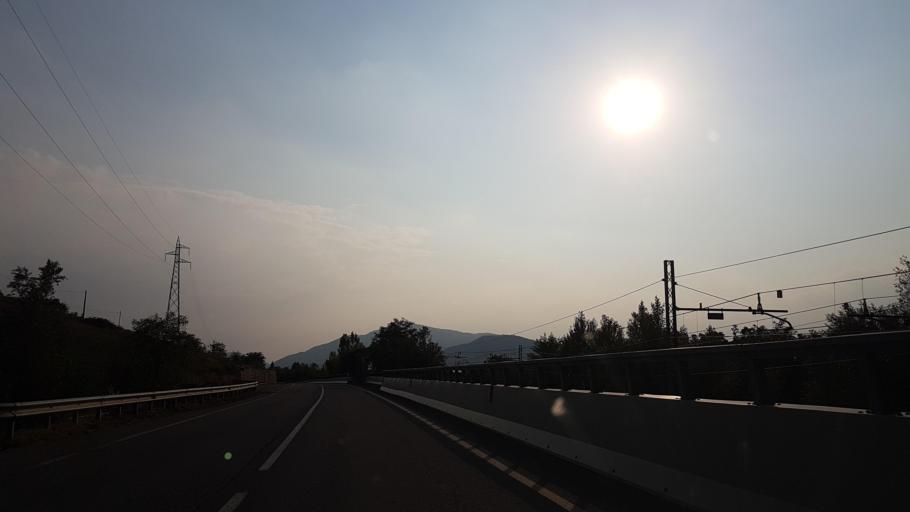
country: IT
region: Emilia-Romagna
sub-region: Provincia di Parma
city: Ramiola
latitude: 44.6744
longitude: 10.0811
